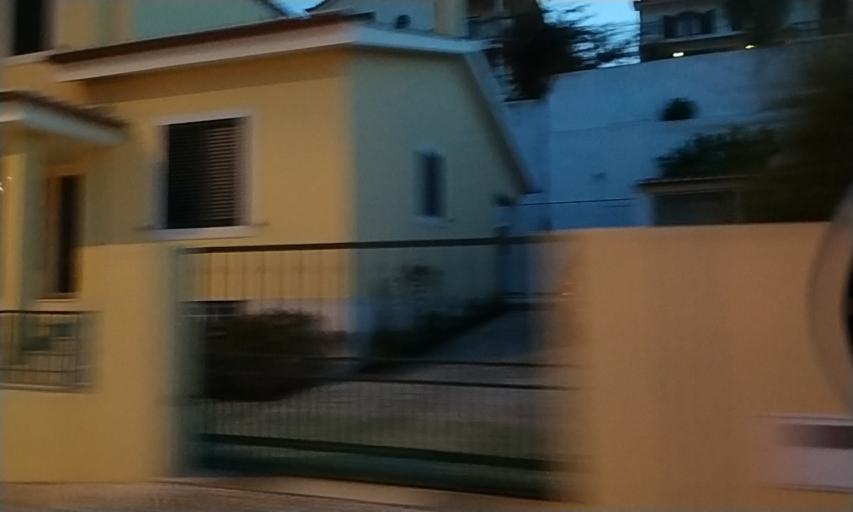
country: PT
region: Setubal
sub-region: Setubal
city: Setubal
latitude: 38.5436
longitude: -8.8955
